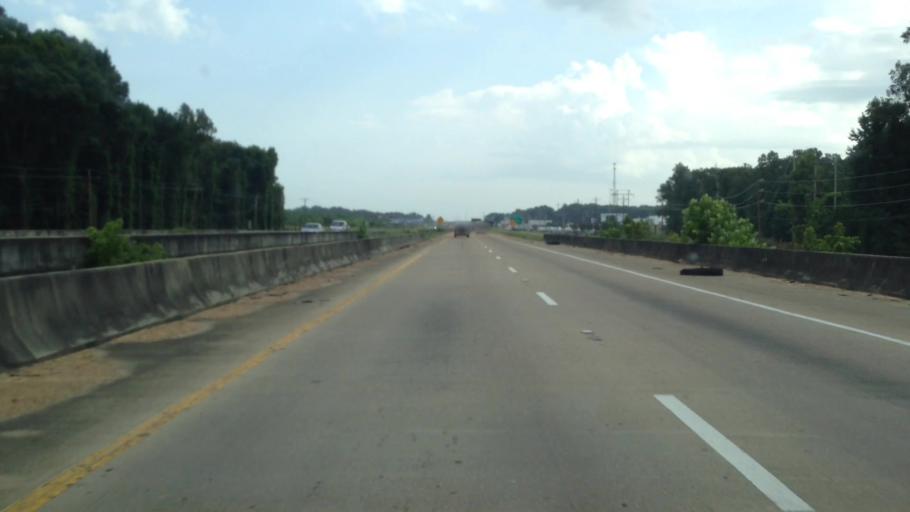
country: US
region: Mississippi
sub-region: Hinds County
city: Byram
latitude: 32.1634
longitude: -90.2703
